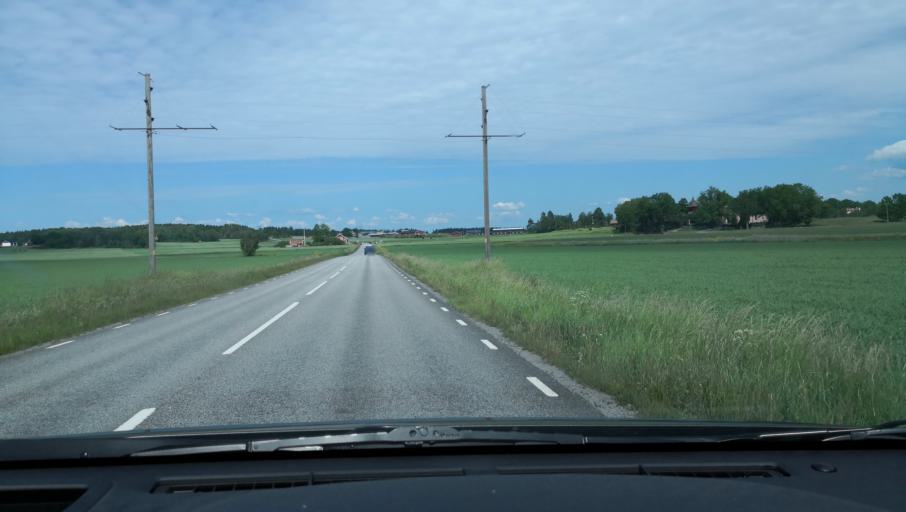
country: SE
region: Stockholm
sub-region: Sigtuna Kommun
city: Sigtuna
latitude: 59.6682
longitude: 17.6936
